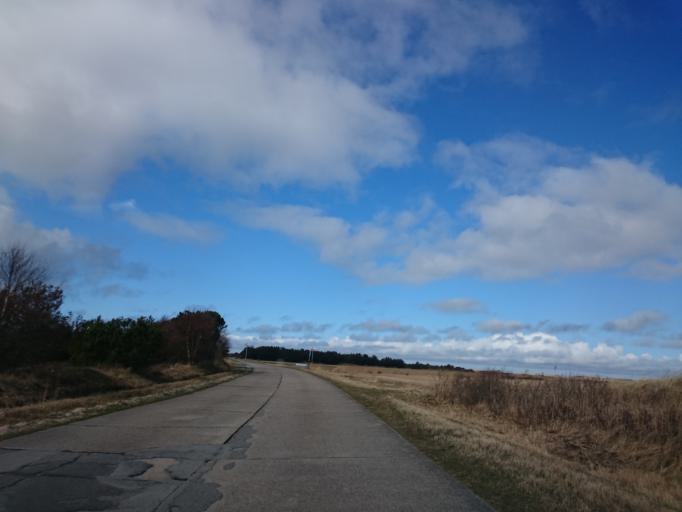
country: DK
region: North Denmark
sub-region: Frederikshavn Kommune
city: Skagen
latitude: 57.6575
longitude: 10.4123
